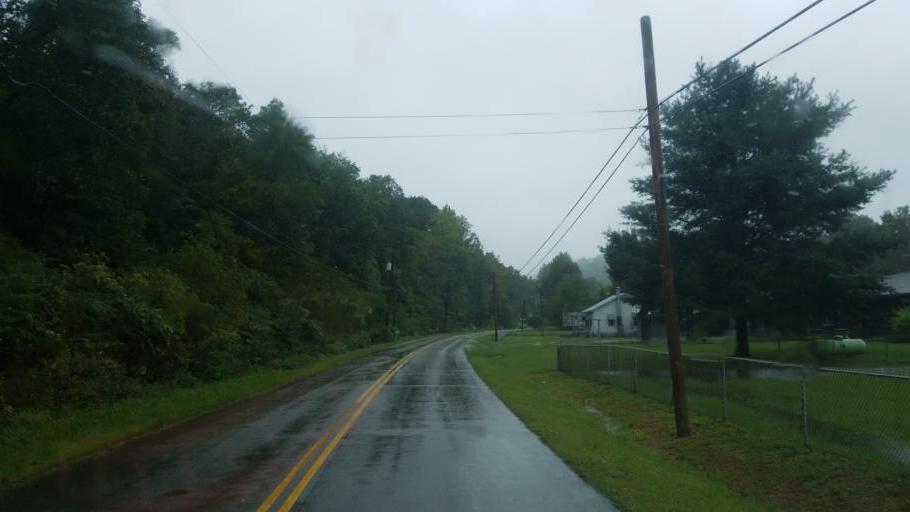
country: US
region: Ohio
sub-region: Scioto County
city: West Portsmouth
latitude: 38.7390
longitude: -83.0713
